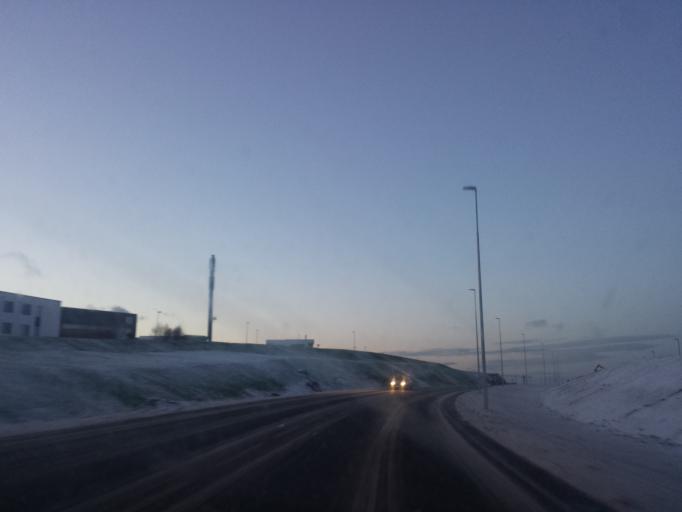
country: IS
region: Capital Region
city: Kopavogur
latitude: 64.0909
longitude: -21.8658
